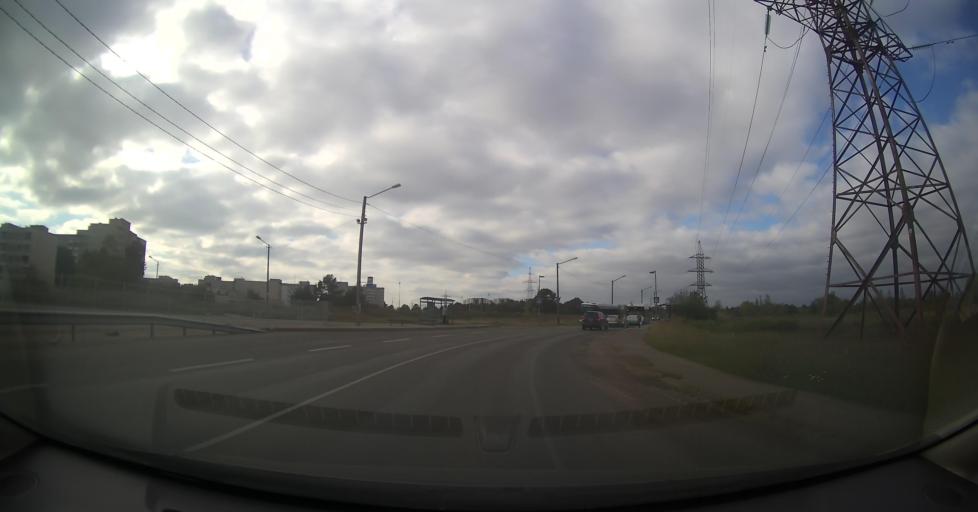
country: EE
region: Harju
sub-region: Tallinna linn
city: Kose
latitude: 59.4297
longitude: 24.8433
